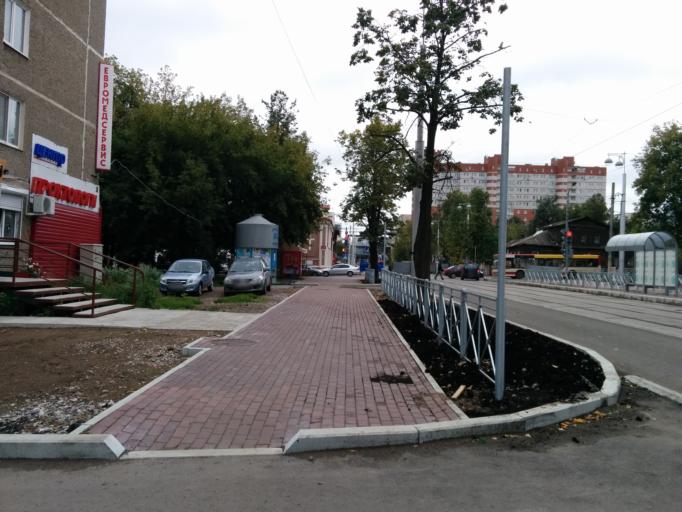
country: RU
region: Perm
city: Perm
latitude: 58.0109
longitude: 56.2568
